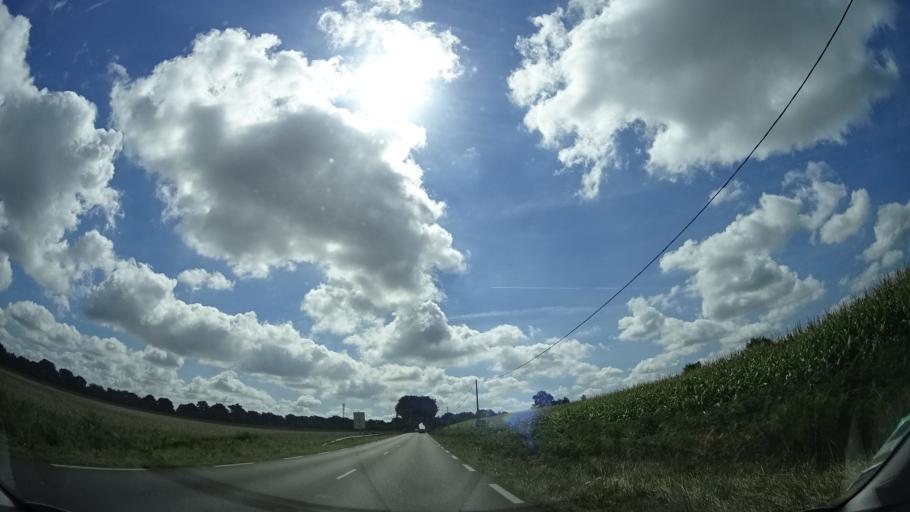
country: FR
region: Pays de la Loire
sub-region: Departement de la Mayenne
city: Meslay-du-Maine
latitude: 47.9594
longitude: -0.5706
